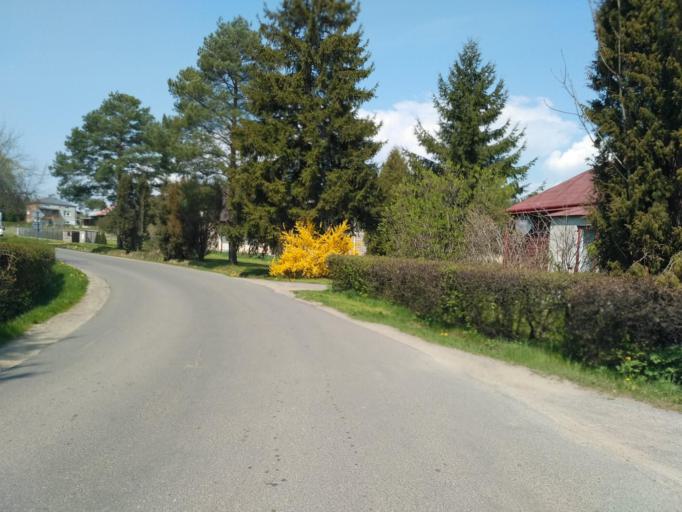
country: PL
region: Subcarpathian Voivodeship
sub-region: Powiat krosnienski
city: Chorkowka
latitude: 49.6605
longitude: 21.6488
